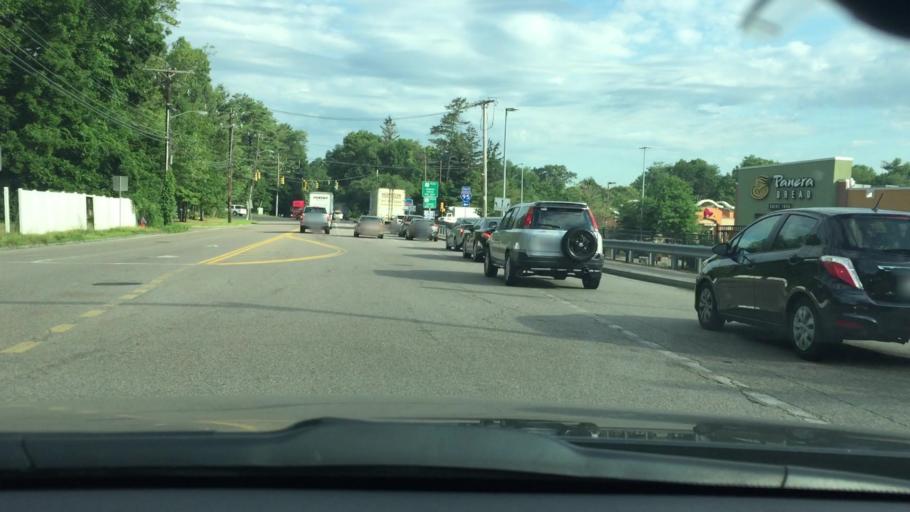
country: US
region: Massachusetts
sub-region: Norfolk County
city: Sharon
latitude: 42.1531
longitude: -71.2043
